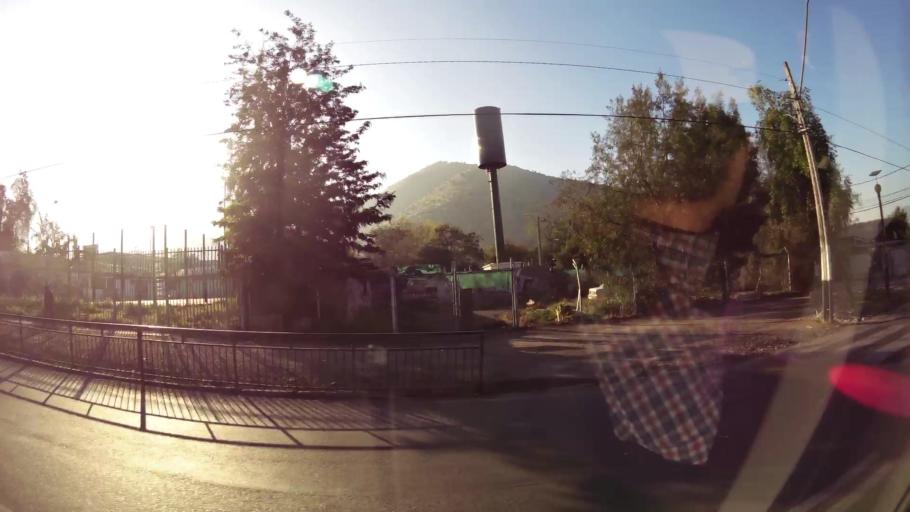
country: CL
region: Santiago Metropolitan
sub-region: Provincia de Chacabuco
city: Chicureo Abajo
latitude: -33.3639
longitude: -70.6326
